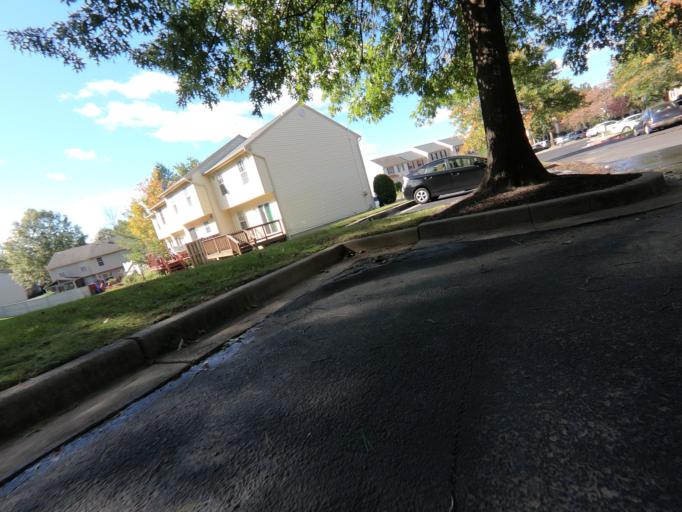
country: US
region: Maryland
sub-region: Howard County
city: Ellicott City
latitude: 39.2613
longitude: -76.8175
